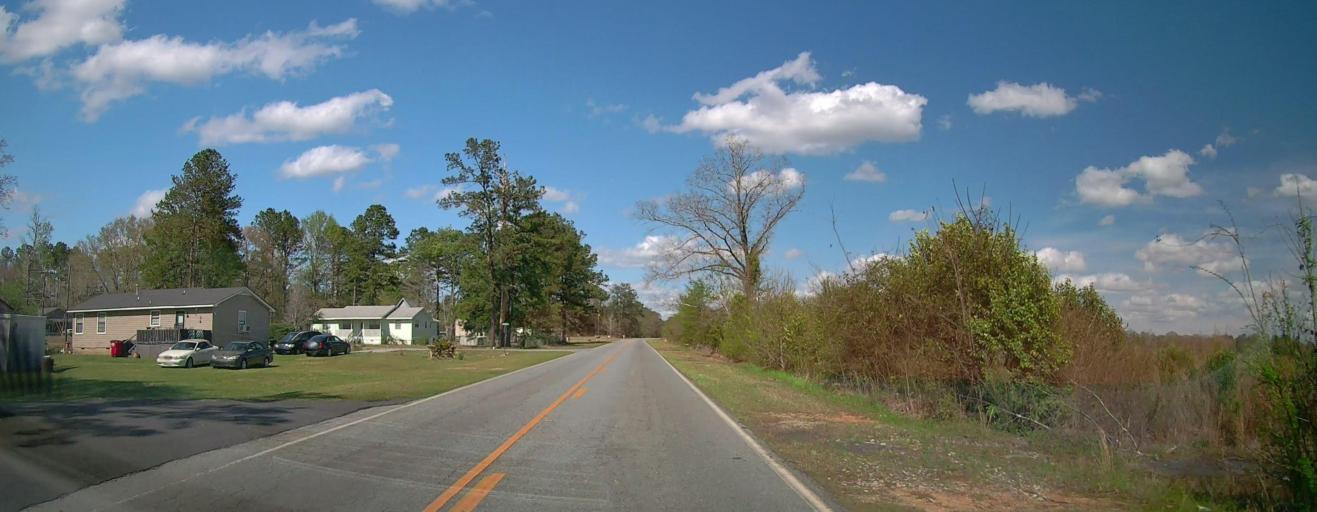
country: US
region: Georgia
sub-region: Bibb County
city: Macon
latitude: 32.8074
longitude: -83.5272
